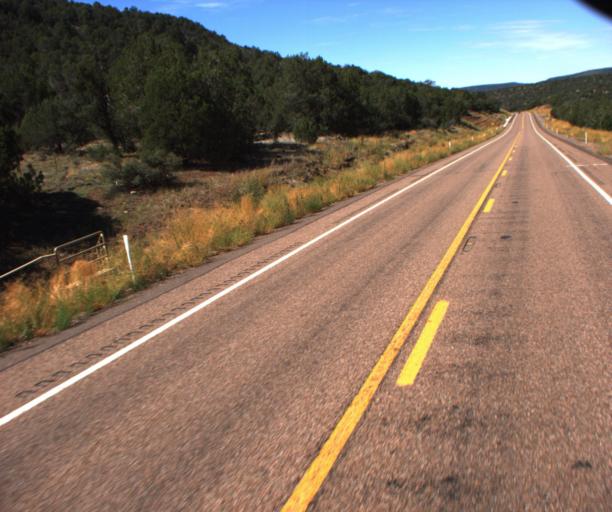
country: US
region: Arizona
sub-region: Navajo County
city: Cibecue
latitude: 33.8938
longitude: -110.3747
